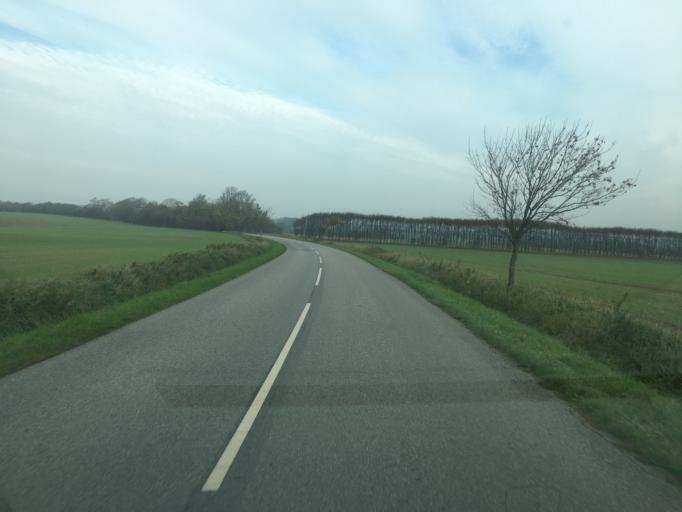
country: DK
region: South Denmark
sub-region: Tonder Kommune
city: Toftlund
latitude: 55.1082
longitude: 9.0887
